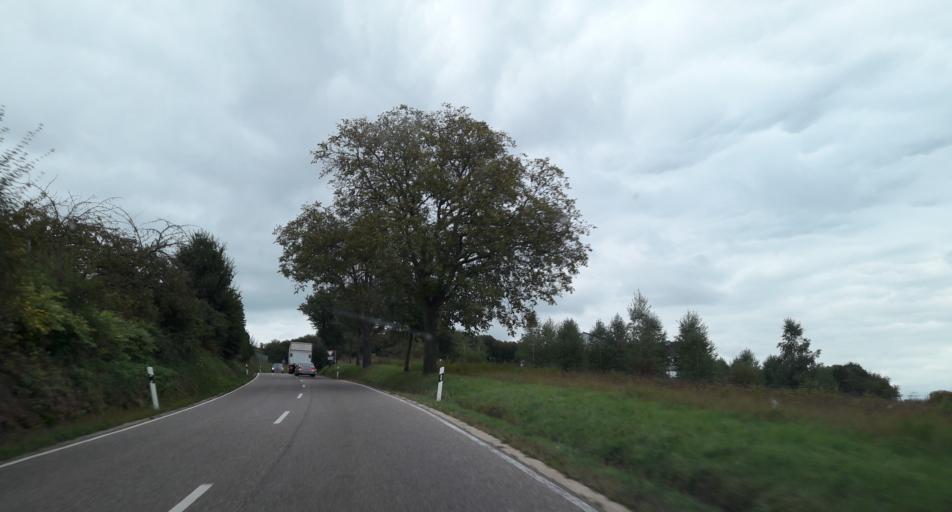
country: DE
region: Baden-Wuerttemberg
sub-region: Regierungsbezirk Stuttgart
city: Kirchardt
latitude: 49.2042
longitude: 8.9974
